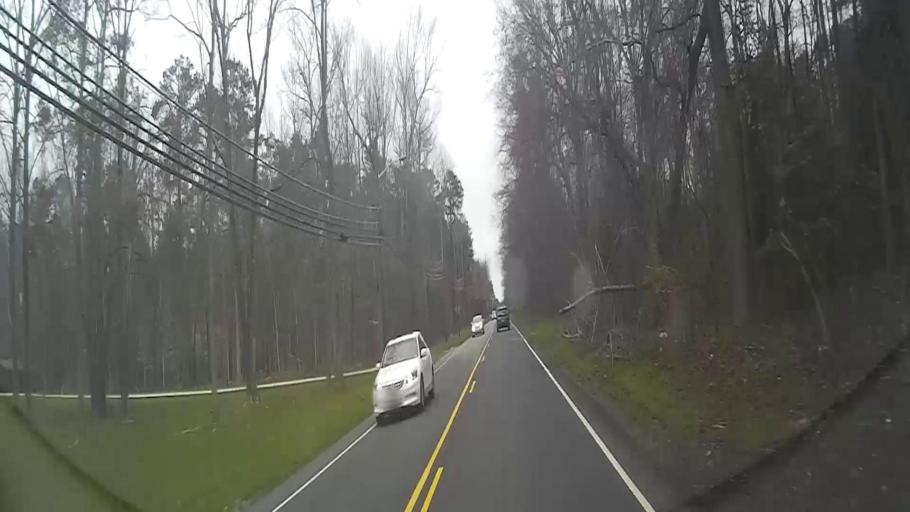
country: US
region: New Jersey
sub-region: Burlington County
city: Medford Lakes
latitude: 39.8754
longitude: -74.8525
